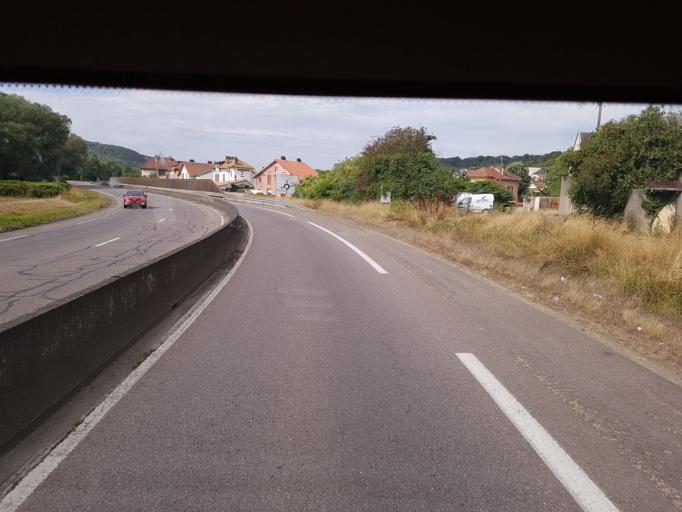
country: FR
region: Lorraine
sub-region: Departement de la Moselle
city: Rosselange
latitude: 49.2581
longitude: 6.0771
